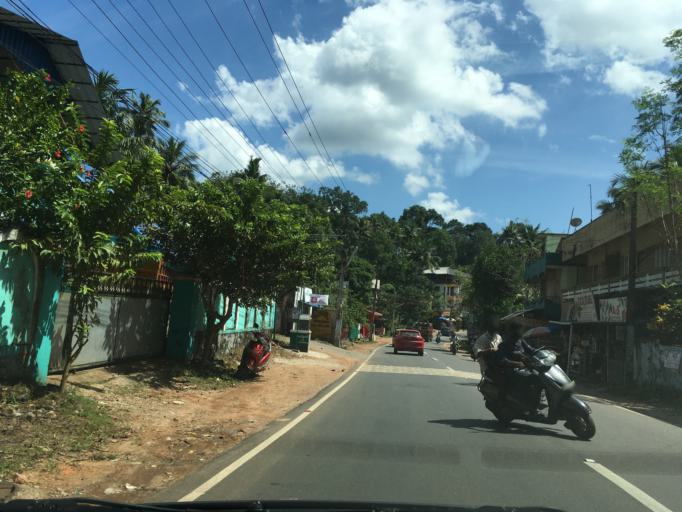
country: IN
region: Kerala
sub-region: Thiruvananthapuram
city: Nedumangad
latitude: 8.5825
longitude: 76.9947
